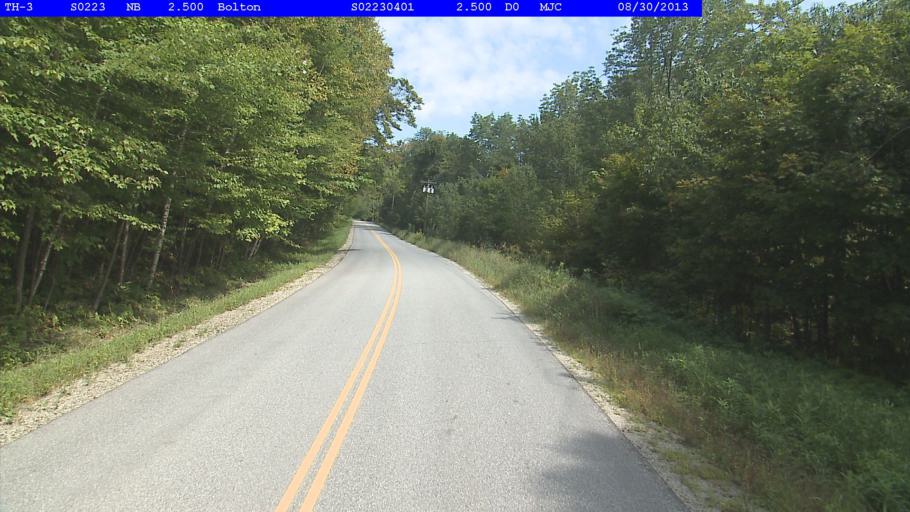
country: US
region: Vermont
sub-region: Washington County
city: Waterbury
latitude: 44.4042
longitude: -72.8740
